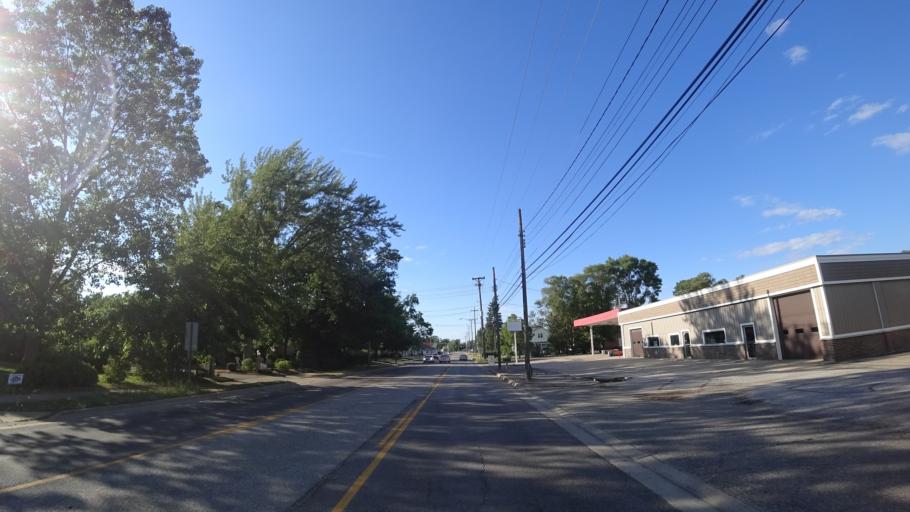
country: US
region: Michigan
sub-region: Ottawa County
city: Holland
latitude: 42.7649
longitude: -86.0971
